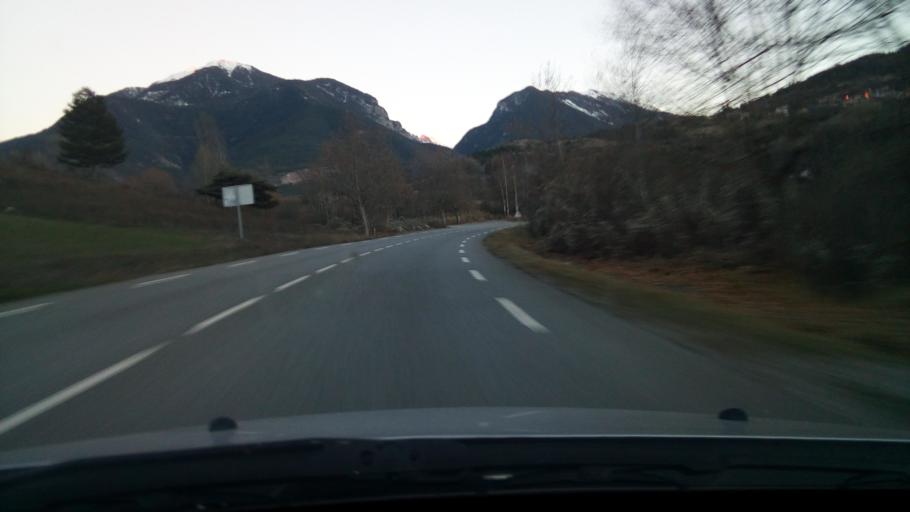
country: FR
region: Provence-Alpes-Cote d'Azur
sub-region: Departement des Hautes-Alpes
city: Guillestre
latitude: 44.6596
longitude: 6.6301
